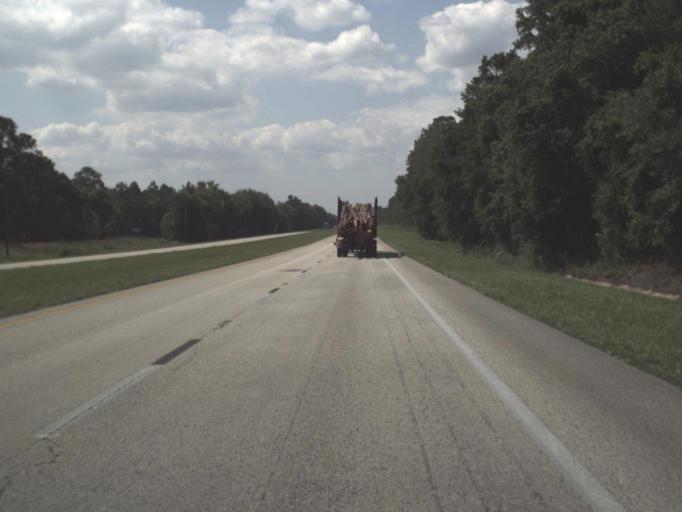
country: US
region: Florida
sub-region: Alachua County
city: Waldo
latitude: 29.7010
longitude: -82.1329
